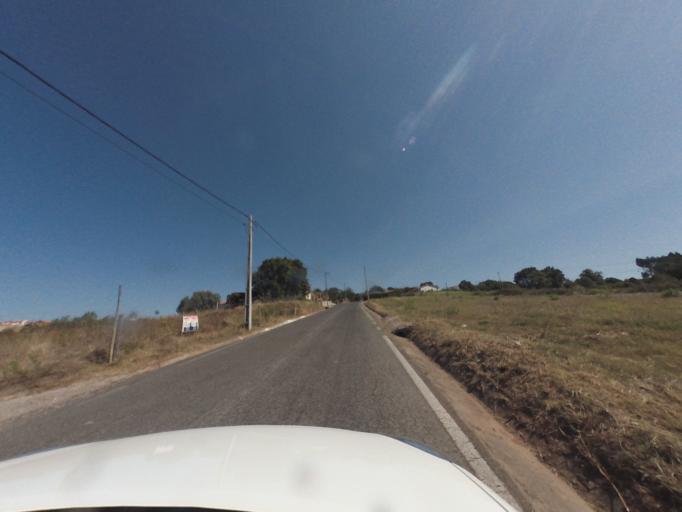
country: PT
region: Leiria
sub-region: Alcobaca
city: Turquel
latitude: 39.4854
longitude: -8.9910
